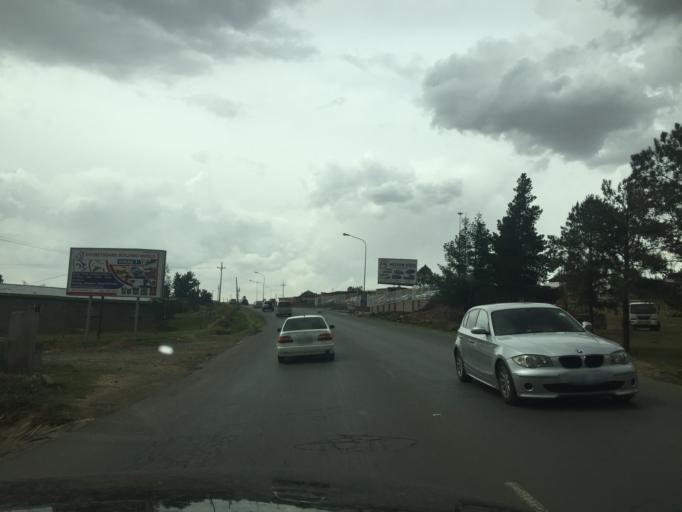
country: LS
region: Maseru
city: Maseru
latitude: -29.2978
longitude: 27.5178
